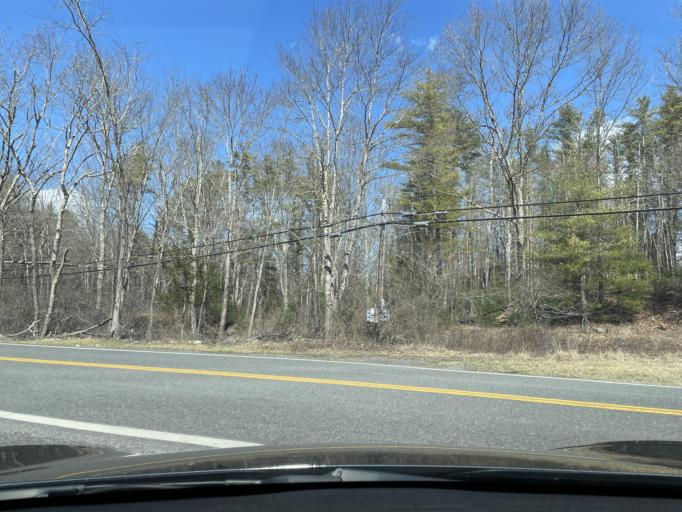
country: US
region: New York
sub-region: Ulster County
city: West Hurley
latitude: 41.9727
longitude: -74.0822
